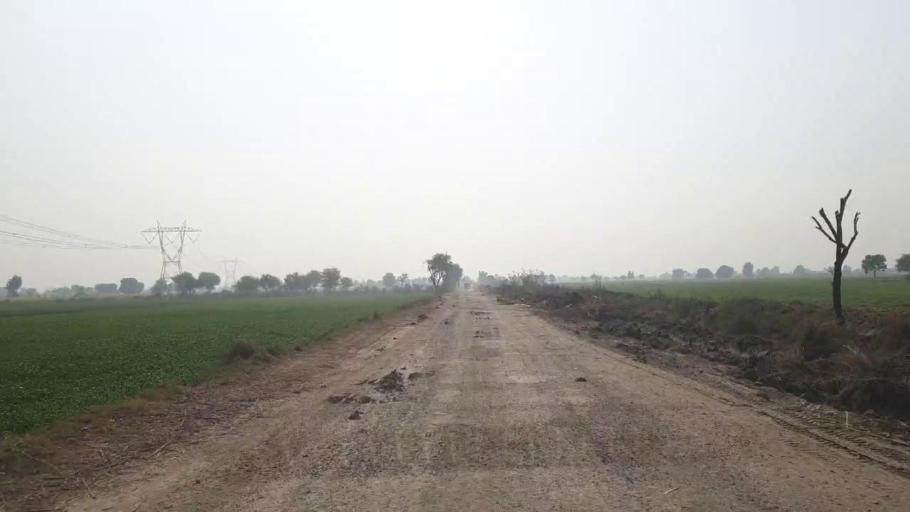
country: PK
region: Sindh
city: Hala
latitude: 25.9364
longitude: 68.4479
